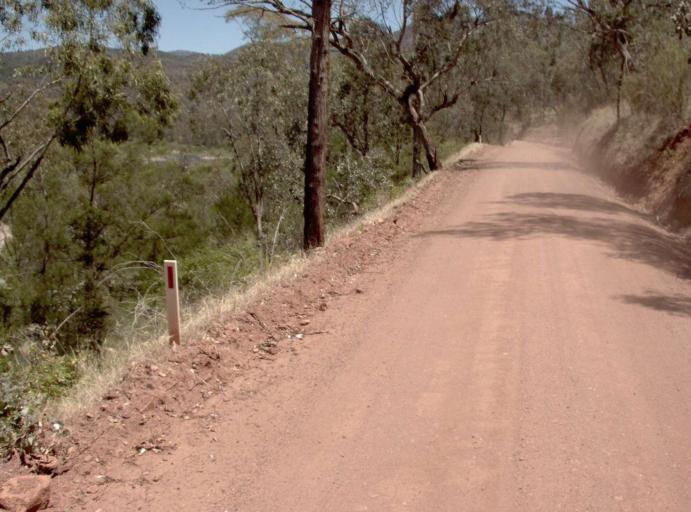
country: AU
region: New South Wales
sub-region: Snowy River
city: Jindabyne
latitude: -36.9180
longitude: 148.4071
